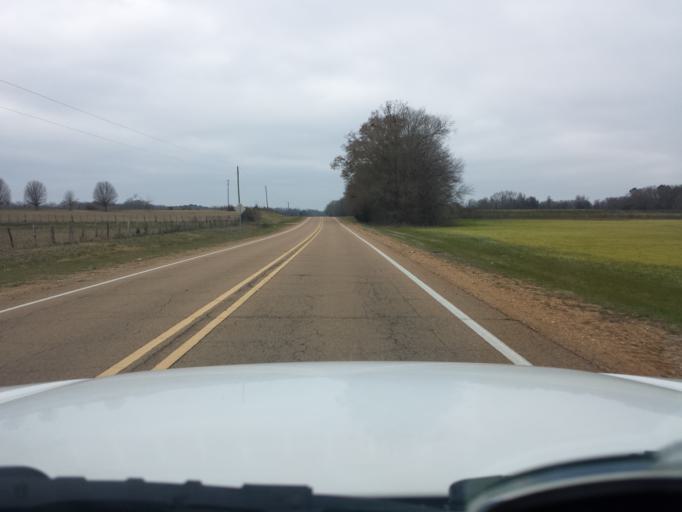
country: US
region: Mississippi
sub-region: Madison County
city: Canton
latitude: 32.7569
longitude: -90.1540
